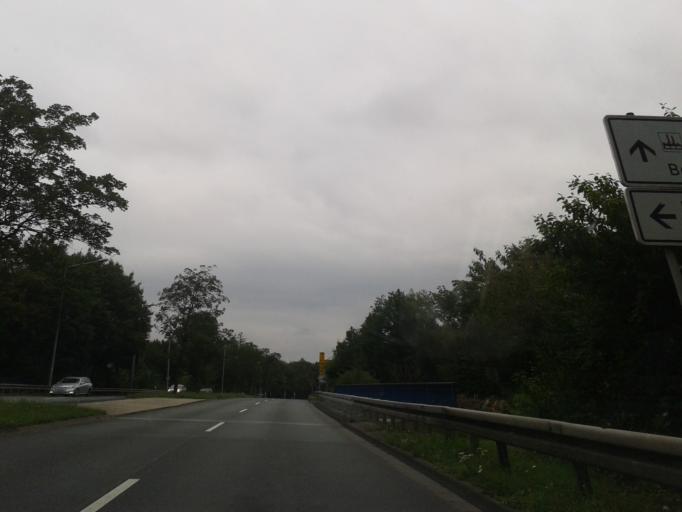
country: DE
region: North Rhine-Westphalia
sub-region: Regierungsbezirk Detmold
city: Paderborn
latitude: 51.7341
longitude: 8.7261
